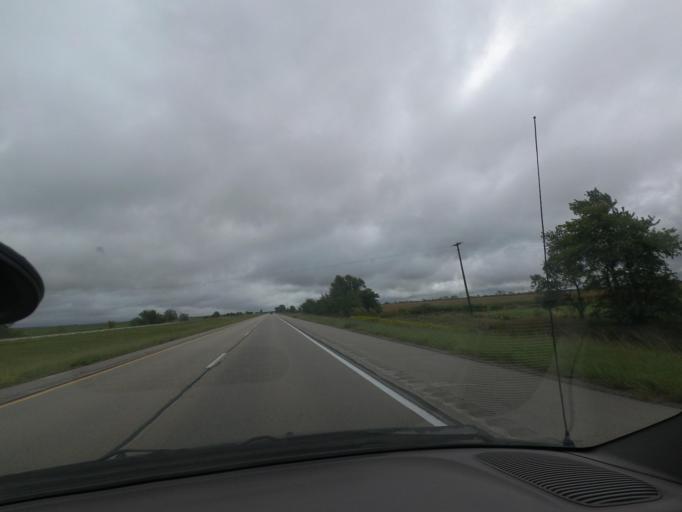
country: US
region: Illinois
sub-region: Piatt County
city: Monticello
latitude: 40.0277
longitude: -88.6623
